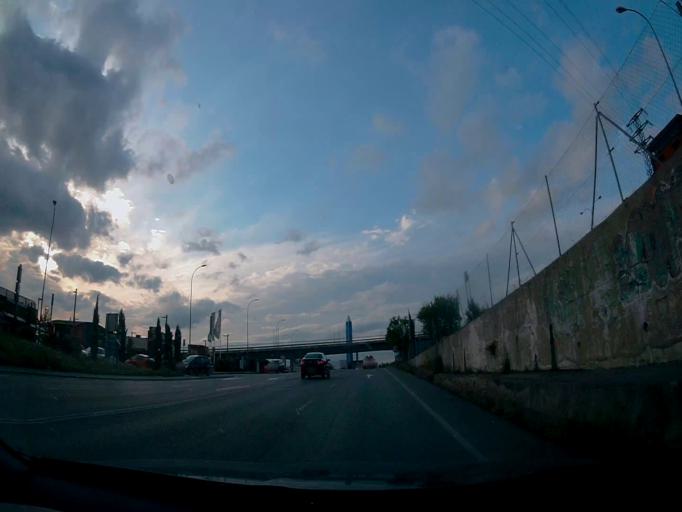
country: ES
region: Madrid
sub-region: Provincia de Madrid
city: Mostoles
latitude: 40.3310
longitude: -3.8838
